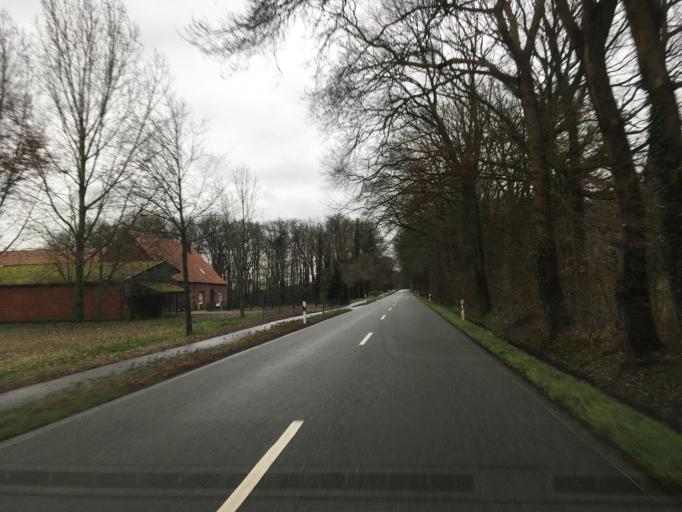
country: DE
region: North Rhine-Westphalia
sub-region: Regierungsbezirk Munster
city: Legden
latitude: 52.0416
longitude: 7.1235
